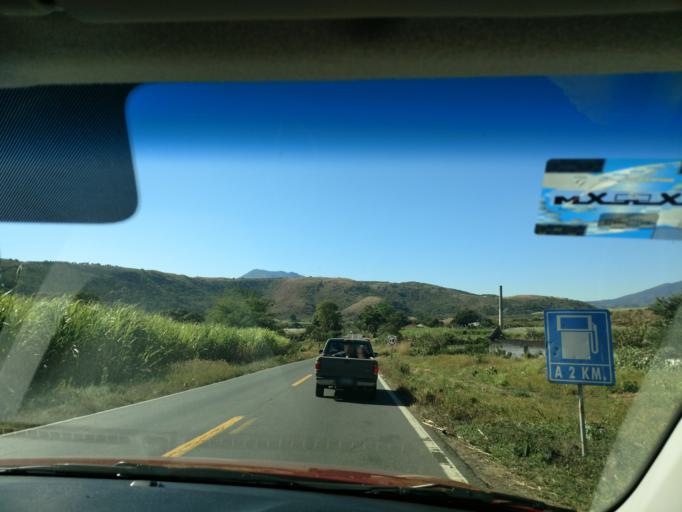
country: MX
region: Nayarit
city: San Pedro Lagunillas
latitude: 21.1523
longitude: -104.6181
